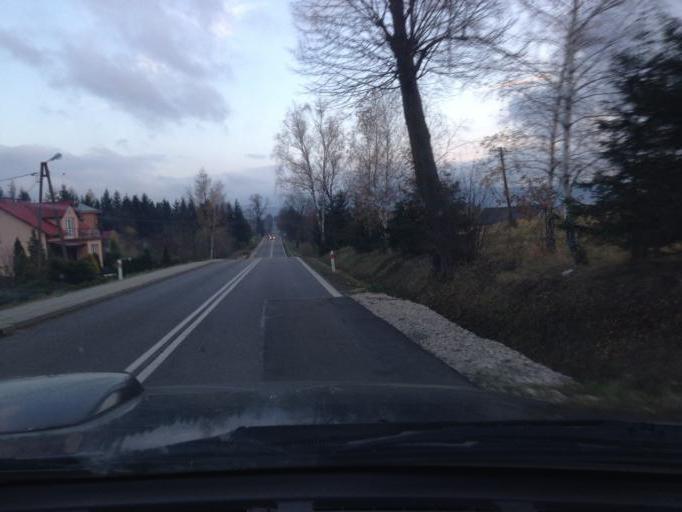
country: PL
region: Subcarpathian Voivodeship
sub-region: Powiat jasielski
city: Nowy Zmigrod
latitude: 49.6376
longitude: 21.5234
